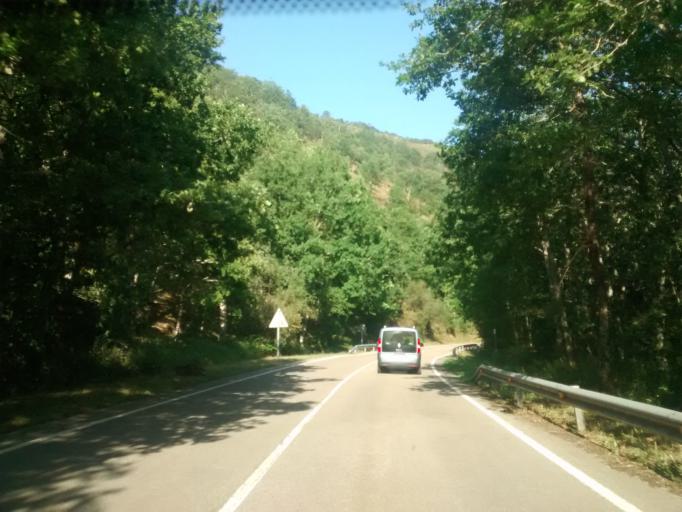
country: ES
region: Cantabria
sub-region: Provincia de Cantabria
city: Ruente
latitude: 43.1529
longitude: -4.2289
